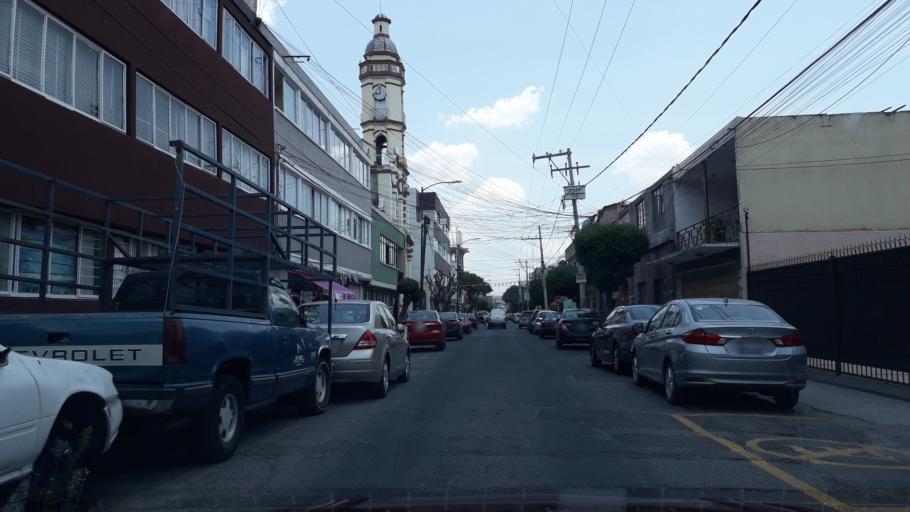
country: MX
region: Puebla
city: Puebla
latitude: 19.0370
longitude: -98.2118
